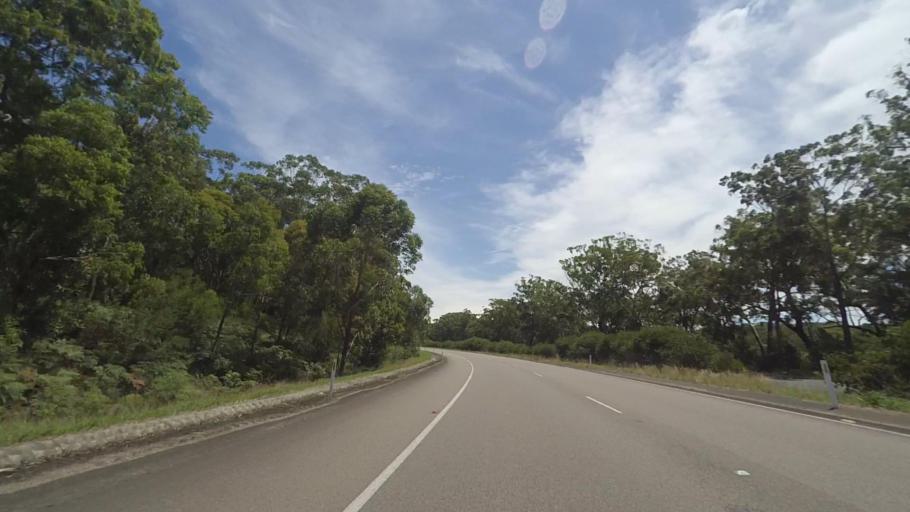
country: AU
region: New South Wales
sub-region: Port Stephens Shire
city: Anna Bay
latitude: -32.7735
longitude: 152.0076
